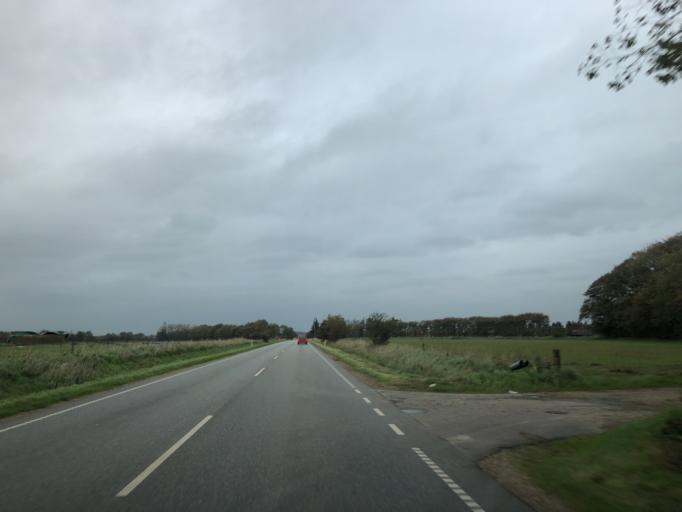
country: DK
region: Central Jutland
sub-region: Herning Kommune
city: Vildbjerg
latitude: 56.2302
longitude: 8.7503
